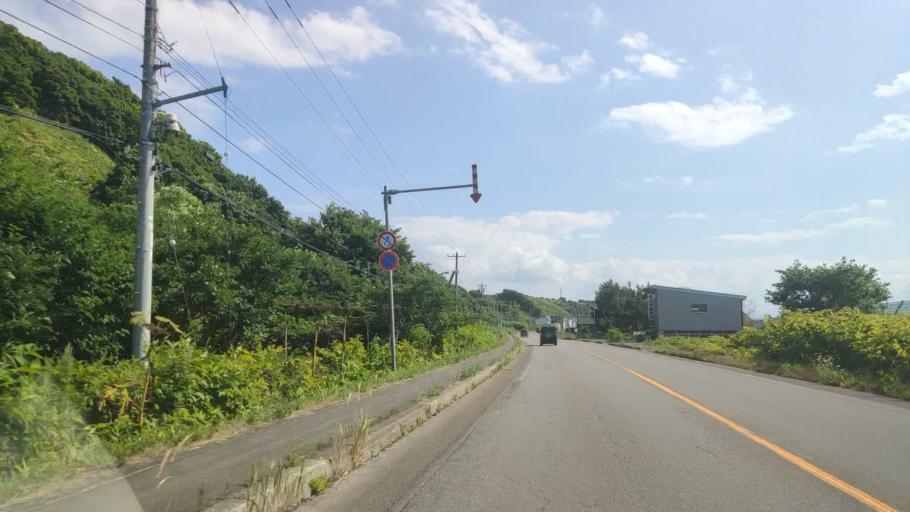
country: JP
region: Hokkaido
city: Rumoi
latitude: 43.9733
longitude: 141.6465
